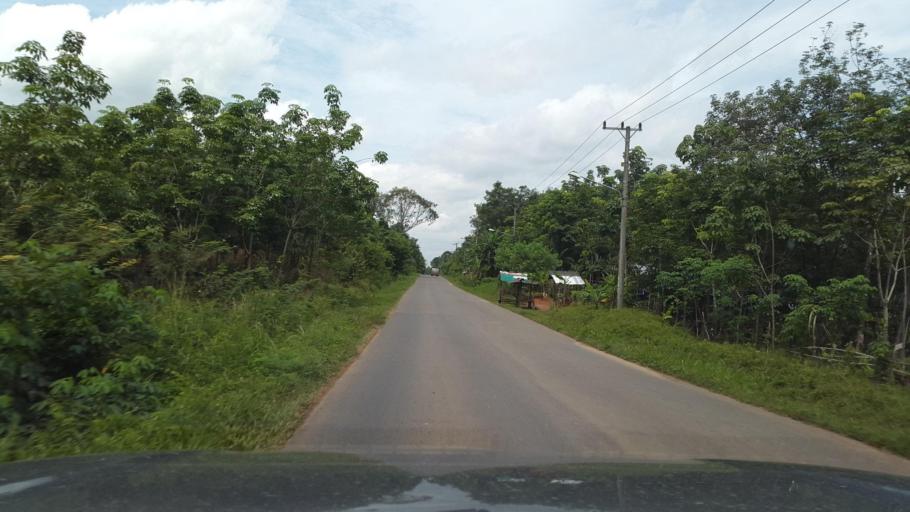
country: ID
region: South Sumatra
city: Gunungmegang Dalam
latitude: -3.3659
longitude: 103.9397
